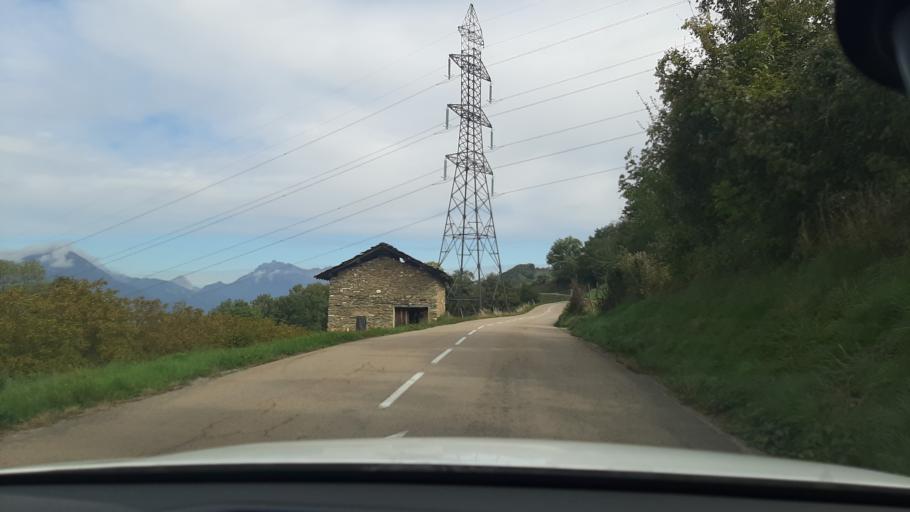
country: FR
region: Rhone-Alpes
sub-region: Departement de l'Isere
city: Pontcharra
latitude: 45.4484
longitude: 6.0522
